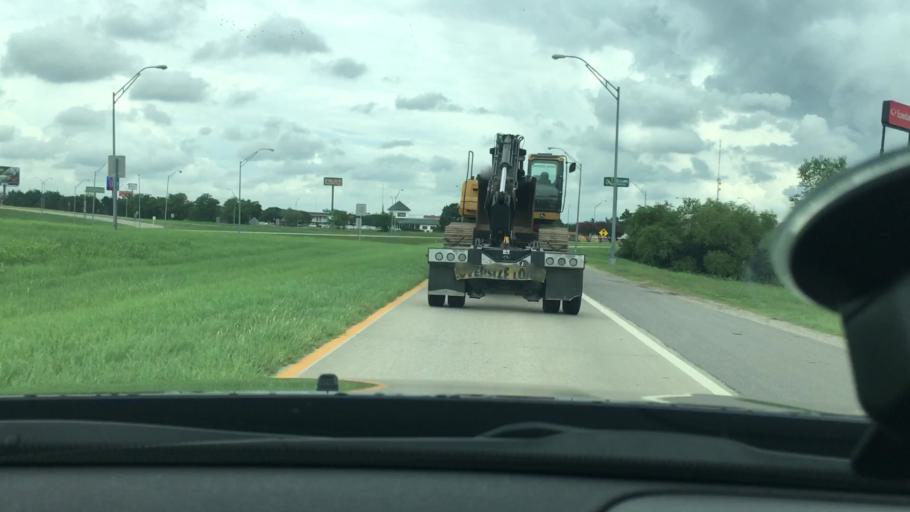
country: US
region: Oklahoma
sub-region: Carter County
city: Ardmore
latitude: 34.1713
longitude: -97.1666
